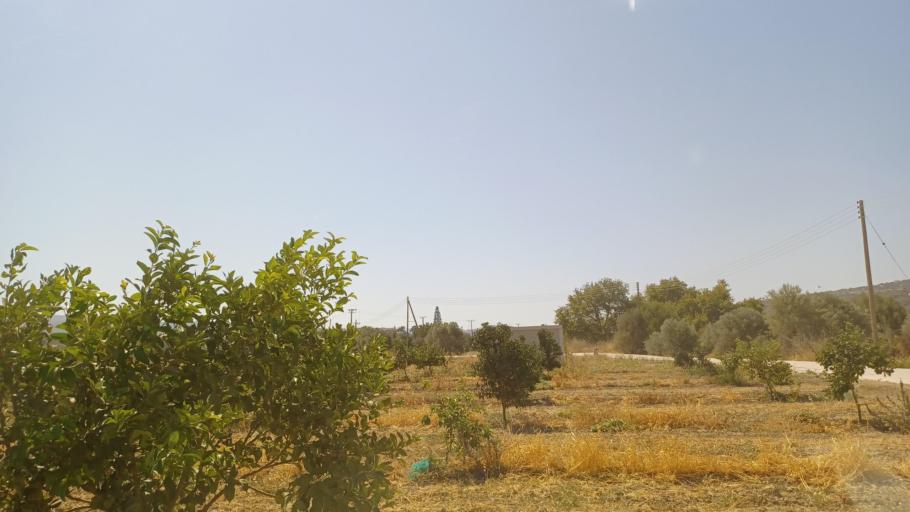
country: CY
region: Pafos
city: Polis
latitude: 35.0109
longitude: 32.4314
